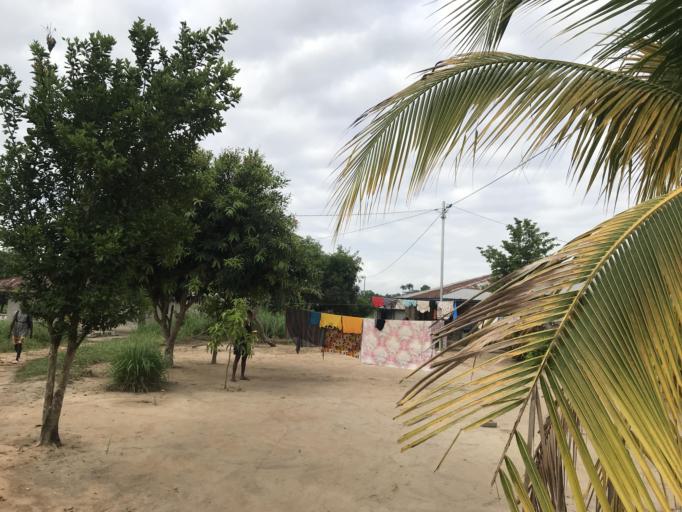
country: SL
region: Eastern Province
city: Pendembu
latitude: 8.0888
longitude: -10.6941
